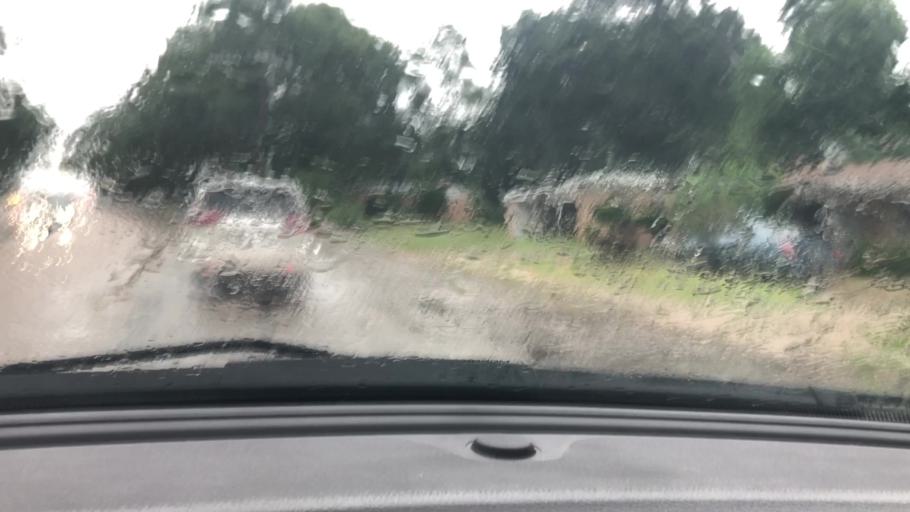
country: US
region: Texas
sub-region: Bowie County
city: Wake Village
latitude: 33.4486
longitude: -94.0802
